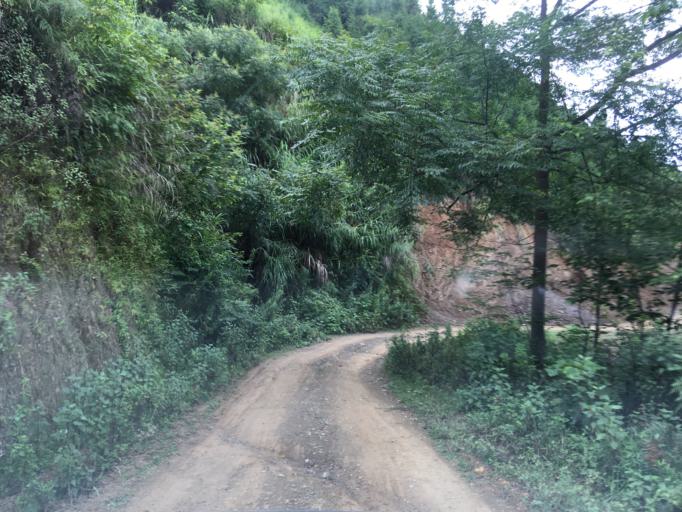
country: CN
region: Guangxi Zhuangzu Zizhiqu
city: Xinzhou
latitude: 24.8738
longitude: 105.8457
